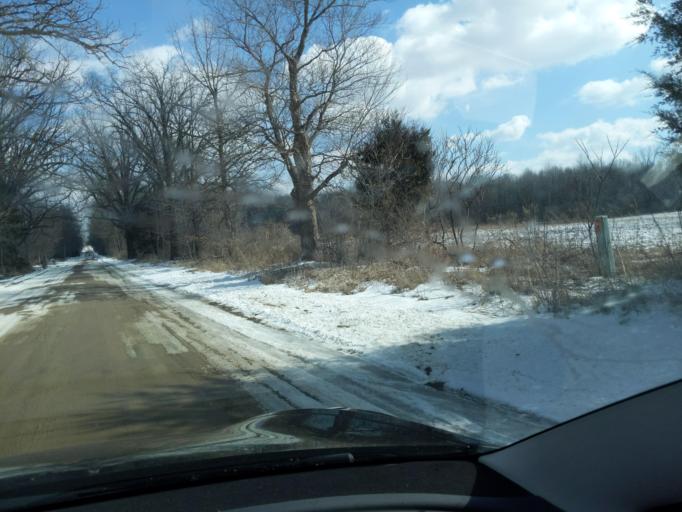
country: US
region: Michigan
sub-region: Livingston County
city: Fowlerville
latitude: 42.6139
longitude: -84.0878
